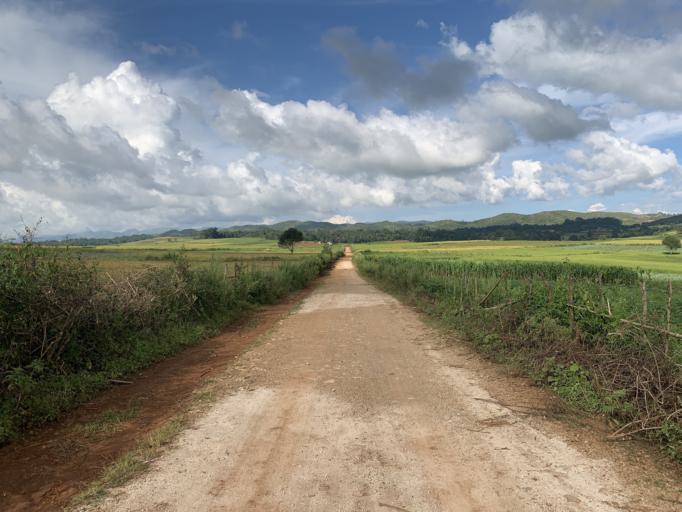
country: MM
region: Shan
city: Taunggyi
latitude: 20.8322
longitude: 96.5643
